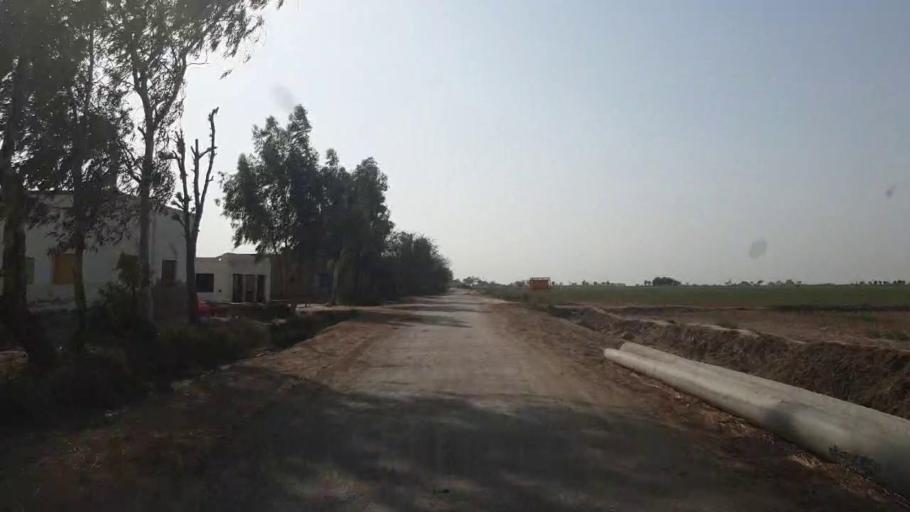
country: PK
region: Sindh
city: Kario
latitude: 24.5764
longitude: 68.5048
